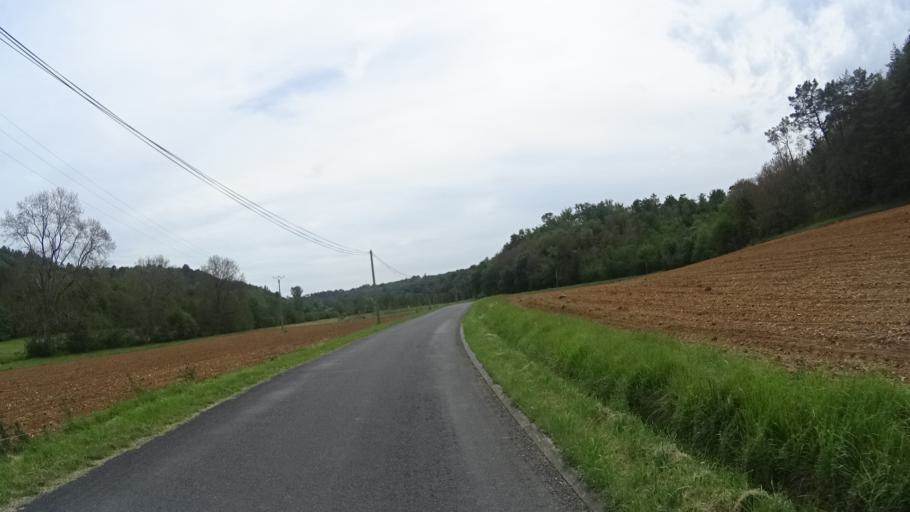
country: FR
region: Aquitaine
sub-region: Departement de la Dordogne
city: Sourzac
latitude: 45.0032
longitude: 0.4579
